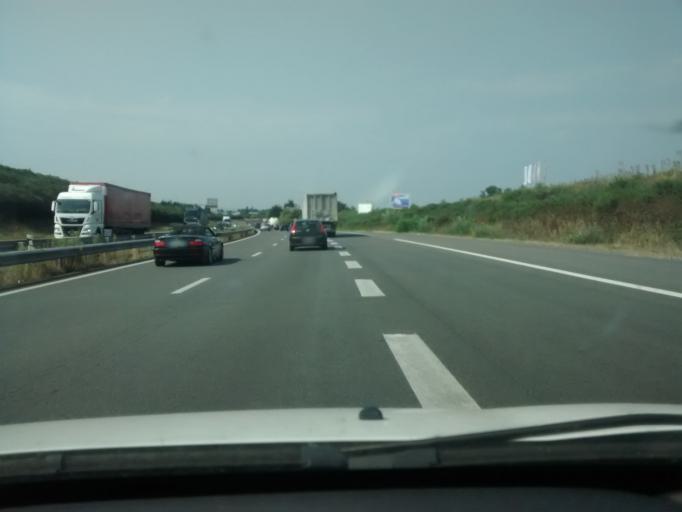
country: FR
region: Pays de la Loire
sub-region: Departement de la Loire-Atlantique
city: Savenay
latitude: 47.3705
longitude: -1.9350
